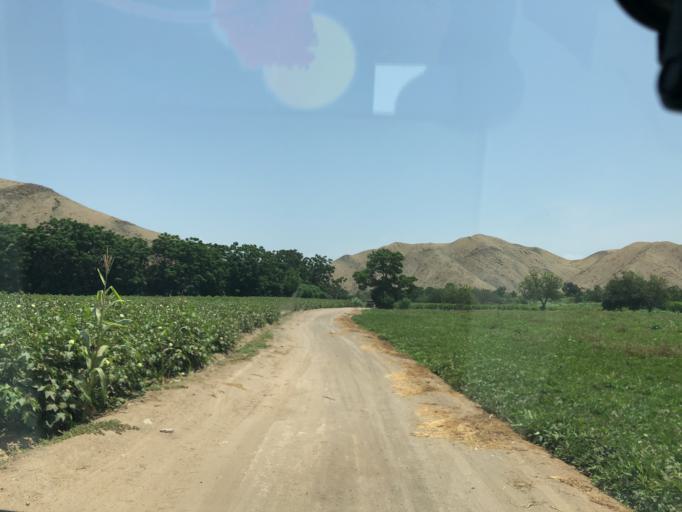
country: PE
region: Lima
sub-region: Provincia de Canete
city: Quilmana
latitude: -12.9809
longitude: -76.4293
